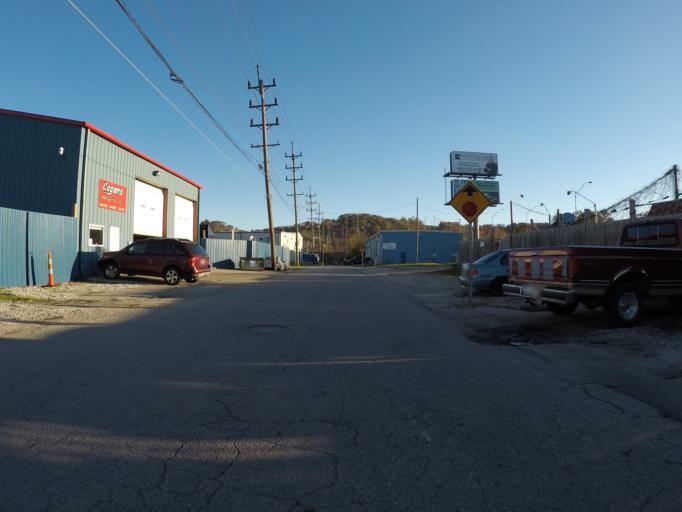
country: US
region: West Virginia
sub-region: Cabell County
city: Huntington
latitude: 38.4080
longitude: -82.4816
